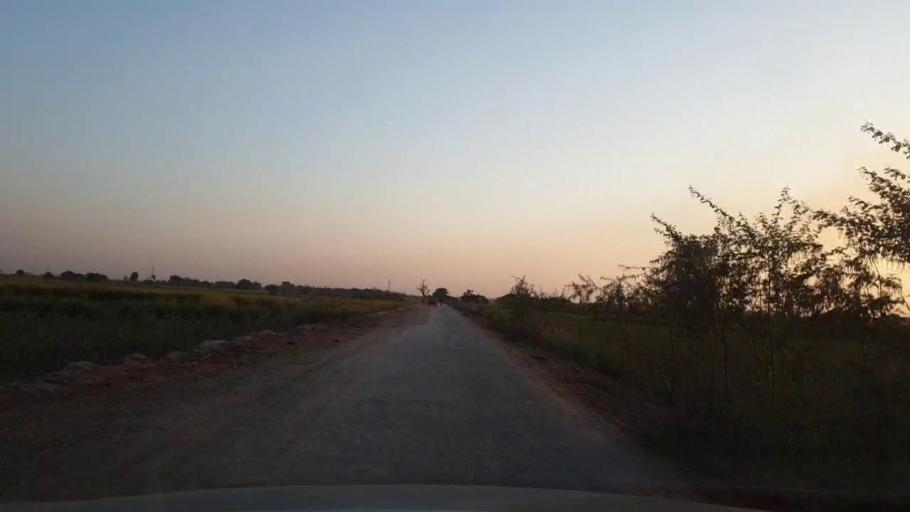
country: PK
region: Sindh
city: Tando Allahyar
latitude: 25.5295
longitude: 68.6254
